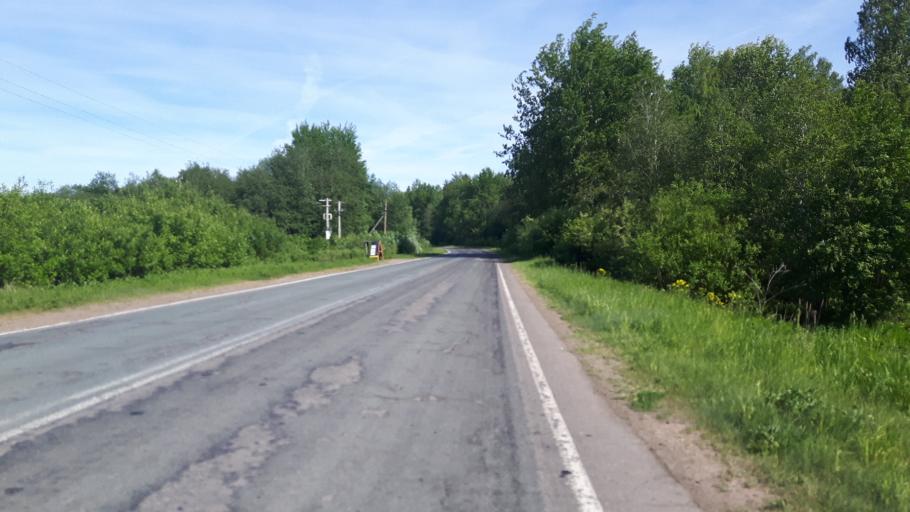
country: RU
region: Leningrad
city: Ivangorod
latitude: 59.4170
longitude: 28.3665
